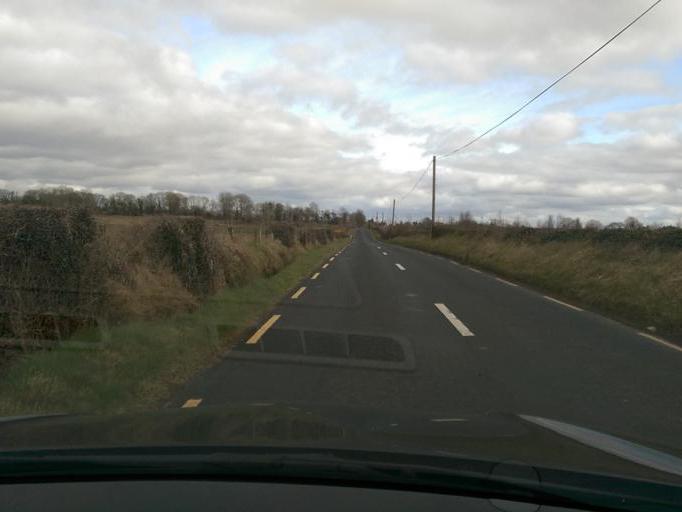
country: IE
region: Connaught
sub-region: County Galway
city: Ballinasloe
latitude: 53.3318
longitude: -8.3550
